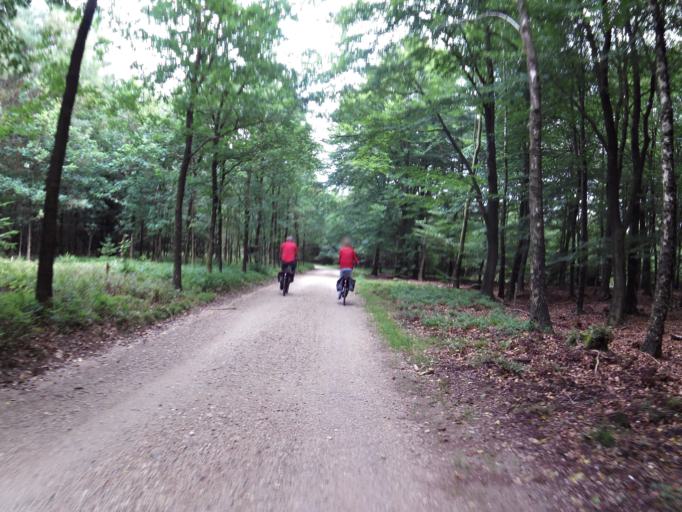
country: NL
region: Gelderland
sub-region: Gemeente Apeldoorn
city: Loenen
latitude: 52.0969
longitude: 6.0045
